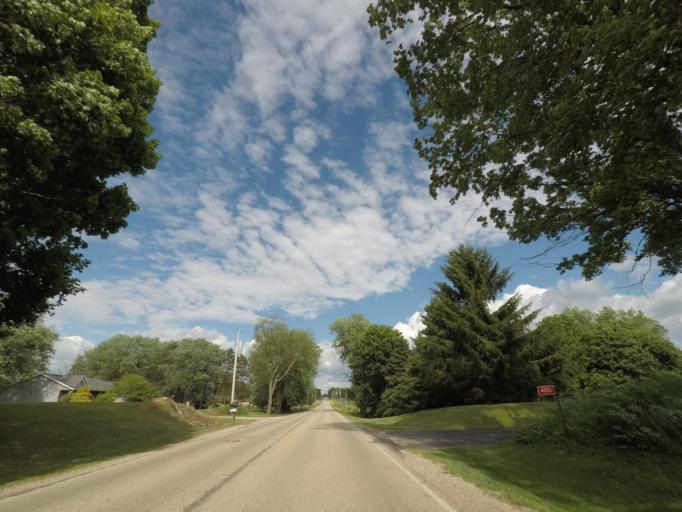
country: US
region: Wisconsin
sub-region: Rock County
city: Janesville
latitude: 42.7011
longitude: -89.0799
